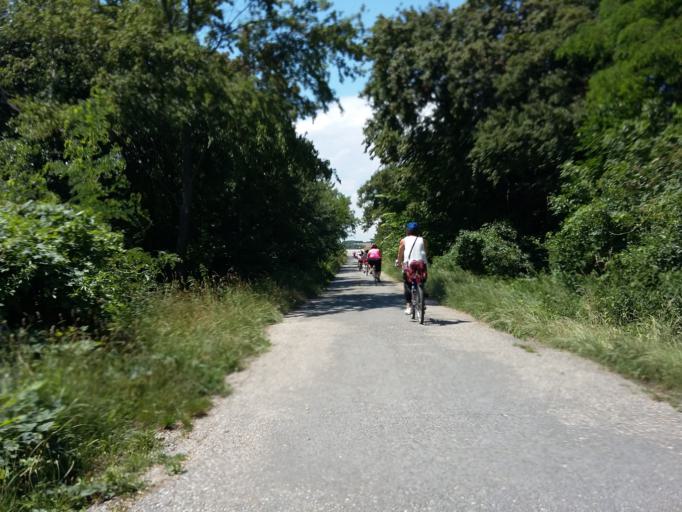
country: AT
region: Lower Austria
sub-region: Politischer Bezirk Bruck an der Leitha
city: Hainburg an der Donau
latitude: 48.2116
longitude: 16.9592
